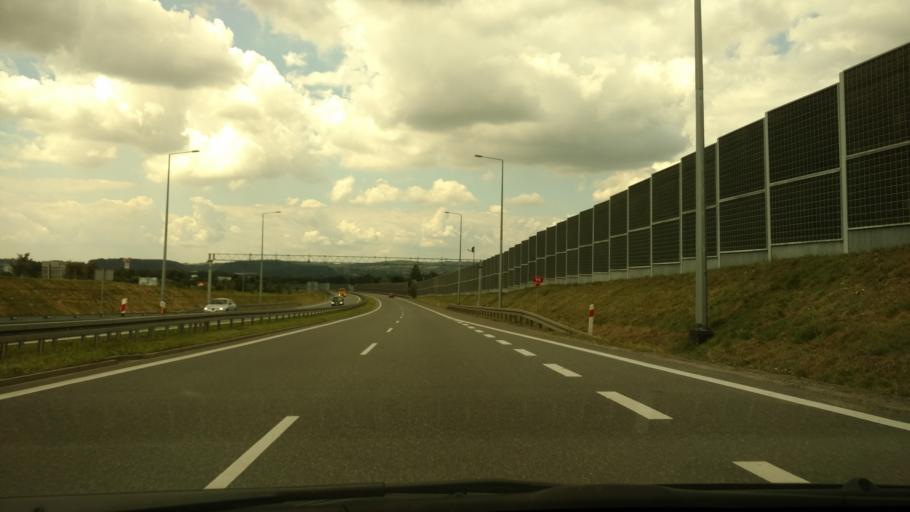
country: PL
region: Lesser Poland Voivodeship
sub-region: Powiat krakowski
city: Modlniczka
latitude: 50.1184
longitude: 19.8614
